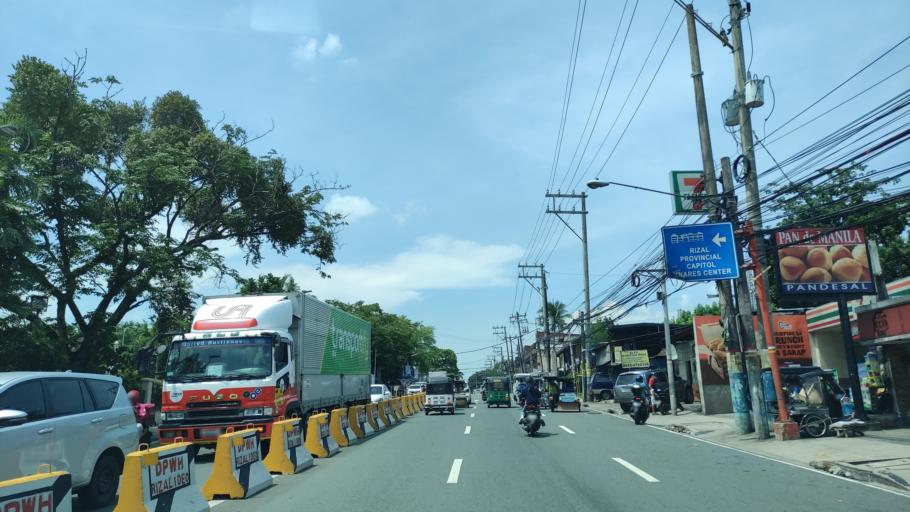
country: PH
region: Calabarzon
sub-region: Province of Rizal
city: Taytay
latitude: 14.5859
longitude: 121.1687
